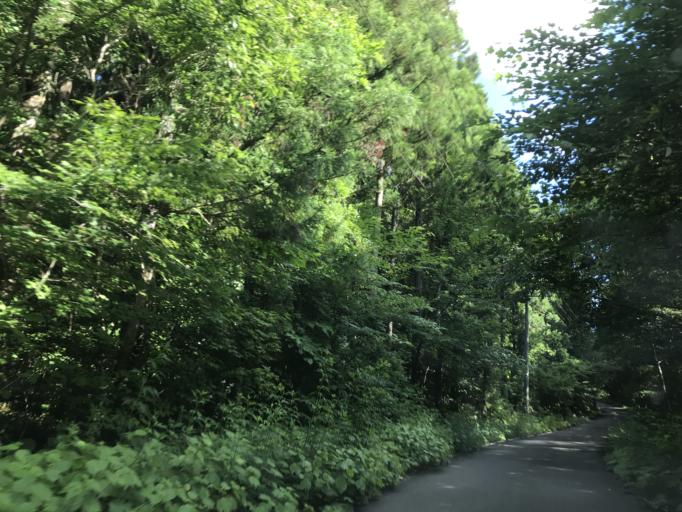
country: JP
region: Iwate
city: Ichinoseki
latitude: 38.8973
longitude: 140.9081
